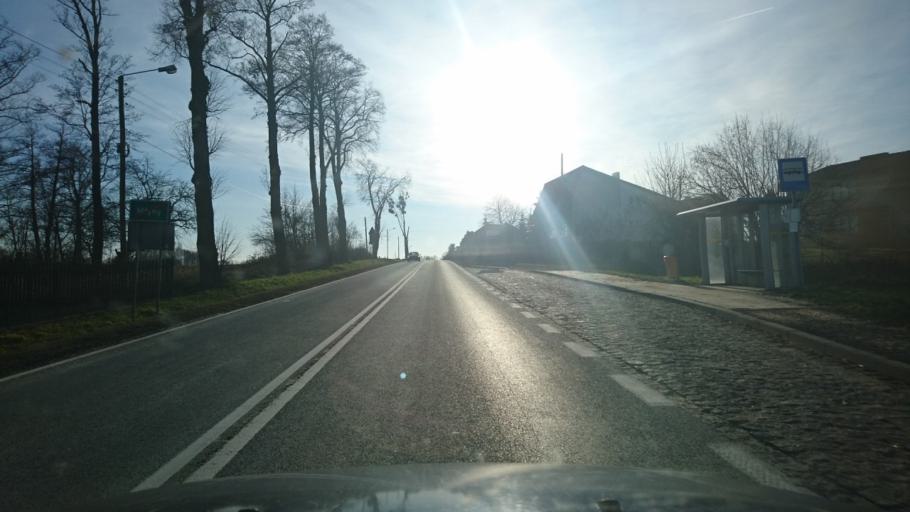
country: PL
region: Opole Voivodeship
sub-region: Powiat oleski
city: Dalachow
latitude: 51.0512
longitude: 18.5981
